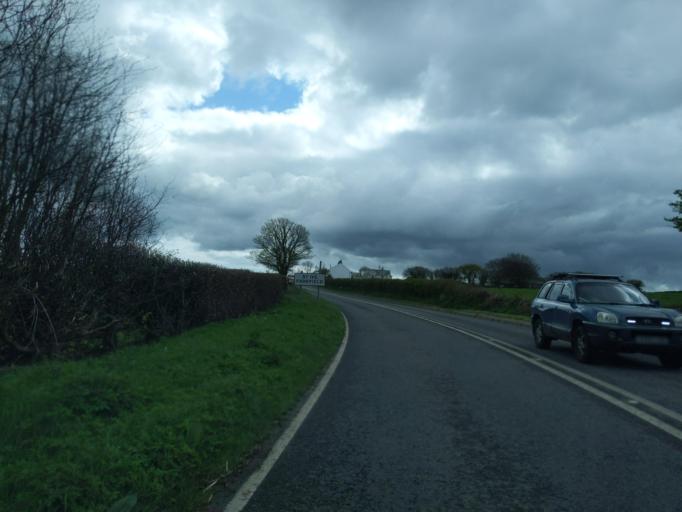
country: GB
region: England
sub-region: Cornwall
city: Pensilva
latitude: 50.4849
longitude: -4.3745
